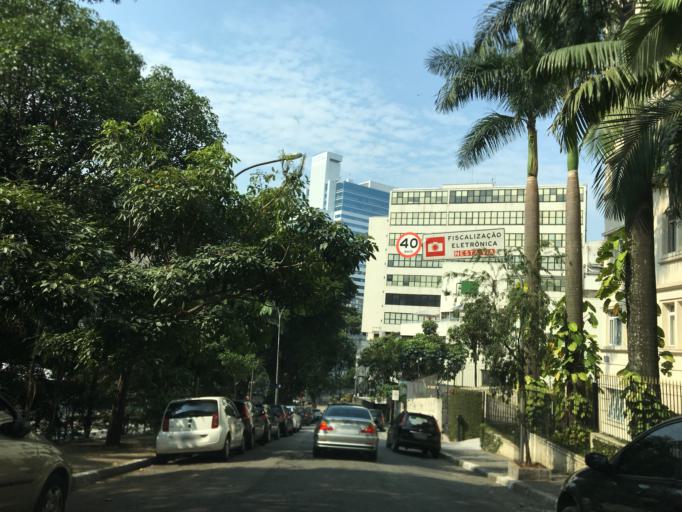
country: BR
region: Sao Paulo
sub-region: Sao Paulo
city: Sao Paulo
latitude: -23.5602
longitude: -46.6544
